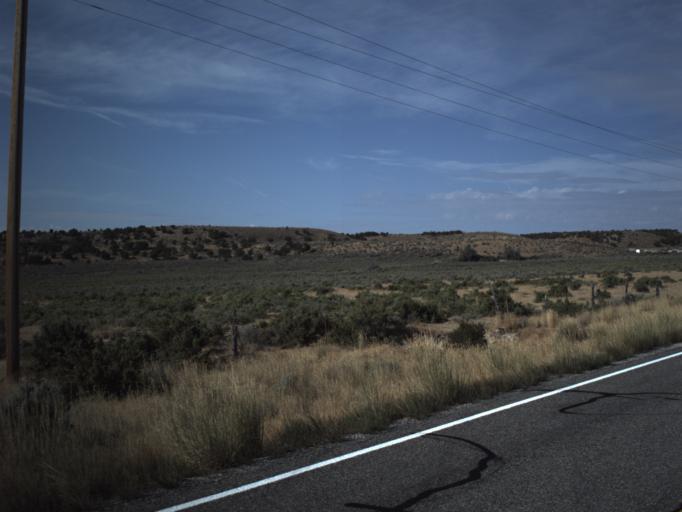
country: US
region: Idaho
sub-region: Cassia County
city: Burley
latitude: 41.8161
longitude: -113.2333
